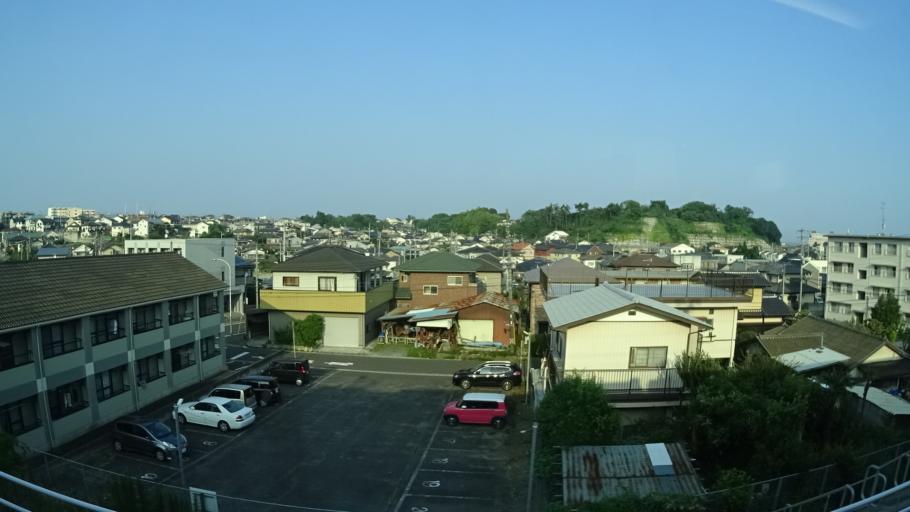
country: JP
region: Ibaraki
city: Funaishikawa
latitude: 36.5008
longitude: 140.6104
